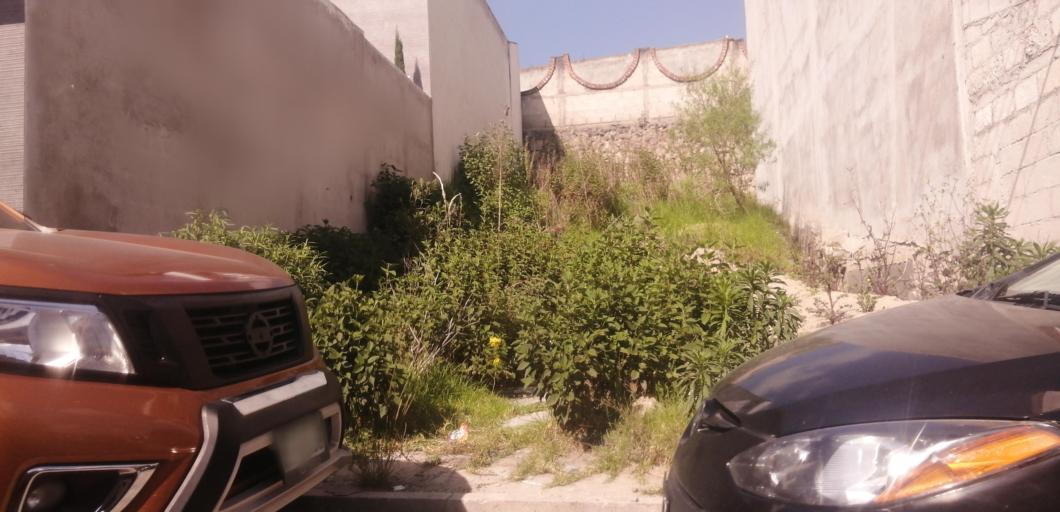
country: GT
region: Quetzaltenango
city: Quetzaltenango
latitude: 14.8398
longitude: -91.5309
